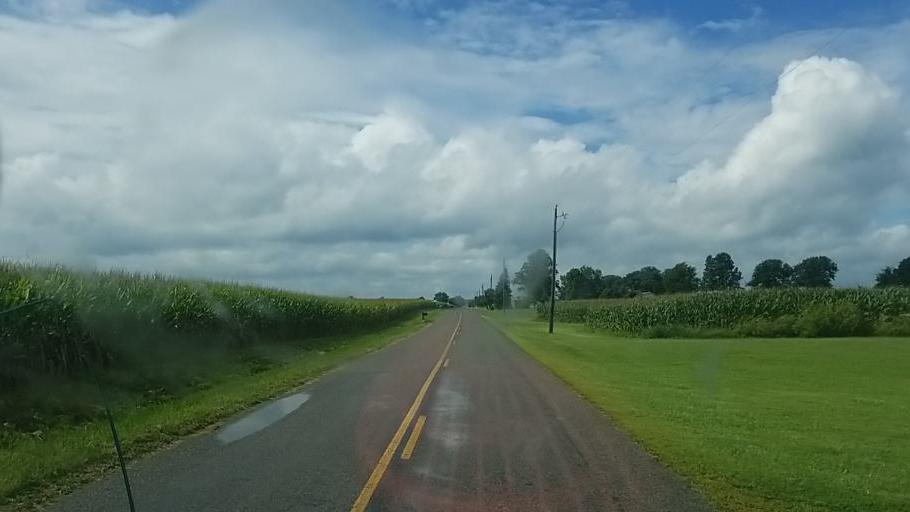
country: US
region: Ohio
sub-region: Hardin County
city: Kenton
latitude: 40.4773
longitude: -83.5103
